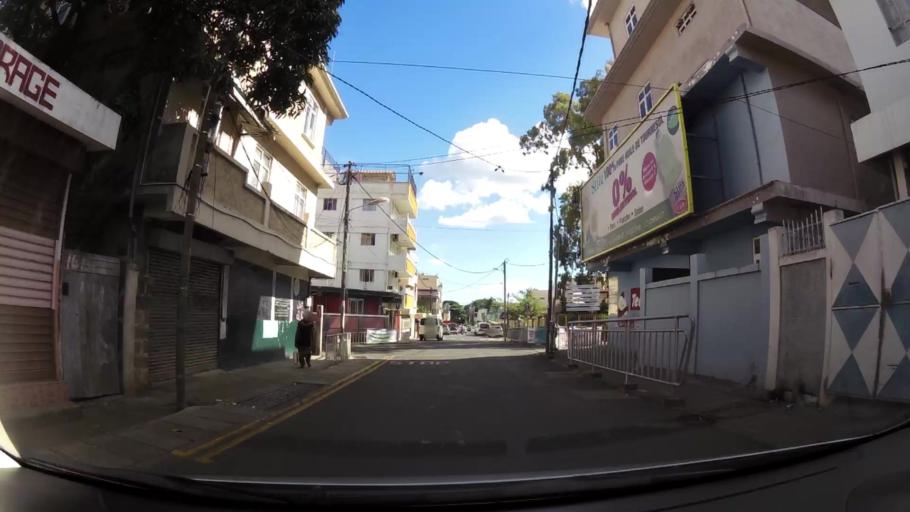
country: MU
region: Port Louis
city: Port Louis
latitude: -20.1605
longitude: 57.5178
